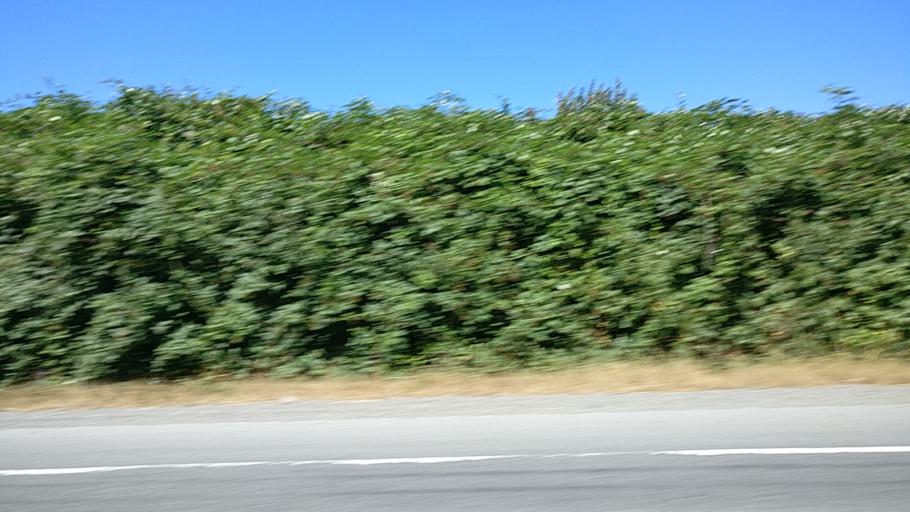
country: CA
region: British Columbia
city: Aldergrove
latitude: 49.0168
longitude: -122.4237
